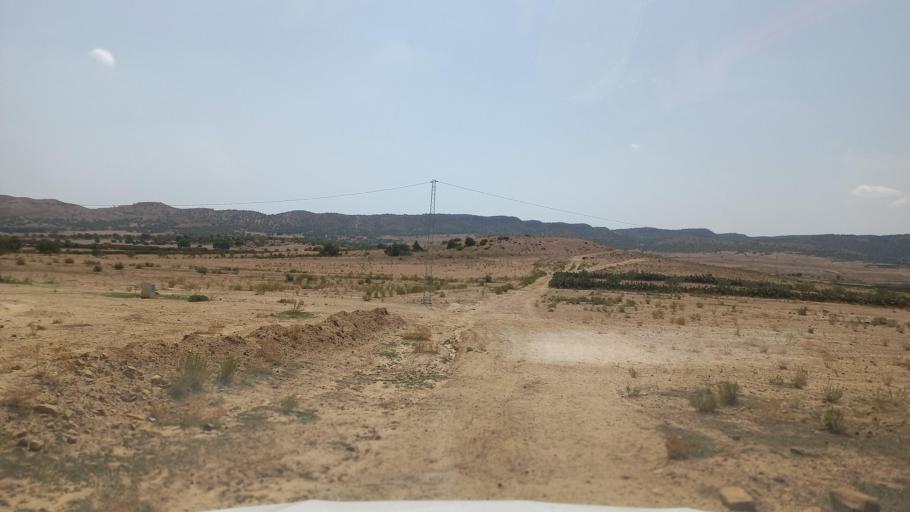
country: TN
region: Al Qasrayn
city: Sbiba
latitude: 35.4002
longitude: 8.9739
